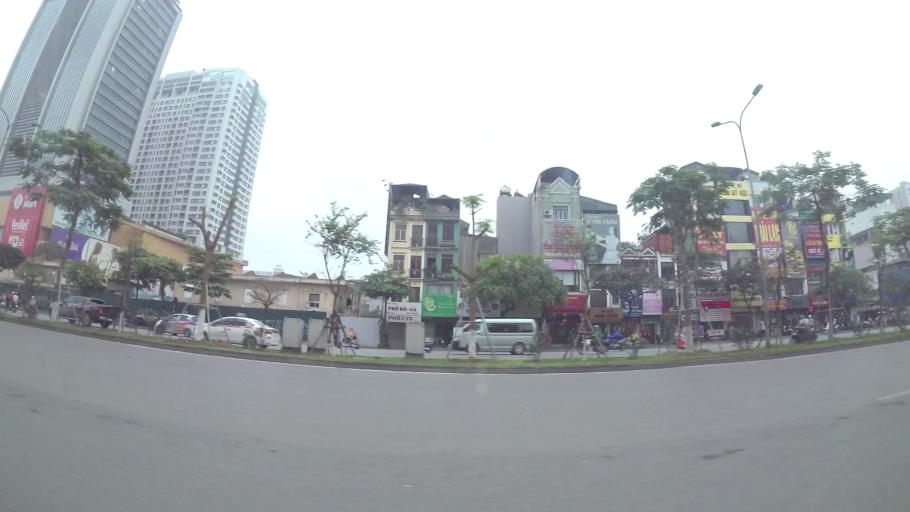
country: VN
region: Ha Noi
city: Dong Da
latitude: 21.0048
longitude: 105.8222
